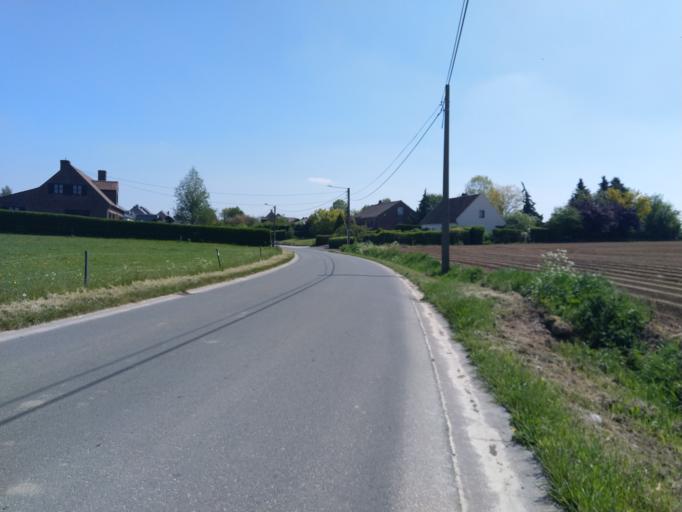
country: BE
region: Wallonia
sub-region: Province du Hainaut
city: Enghien
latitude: 50.6627
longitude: 4.0536
